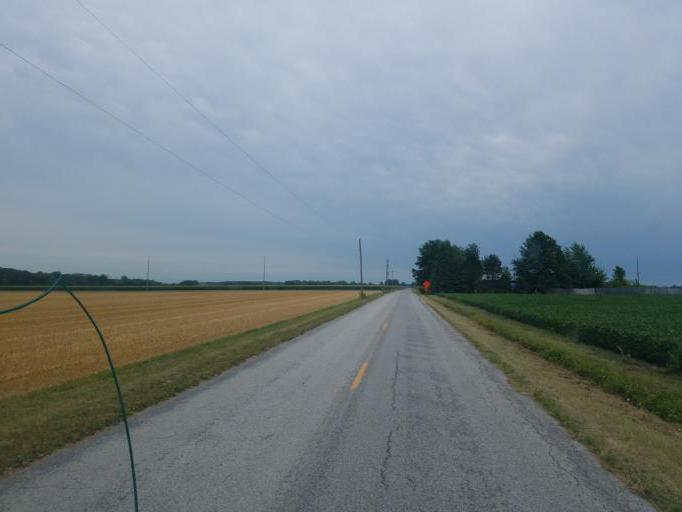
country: US
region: Ohio
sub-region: Defiance County
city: Hicksville
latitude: 41.2373
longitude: -84.7579
